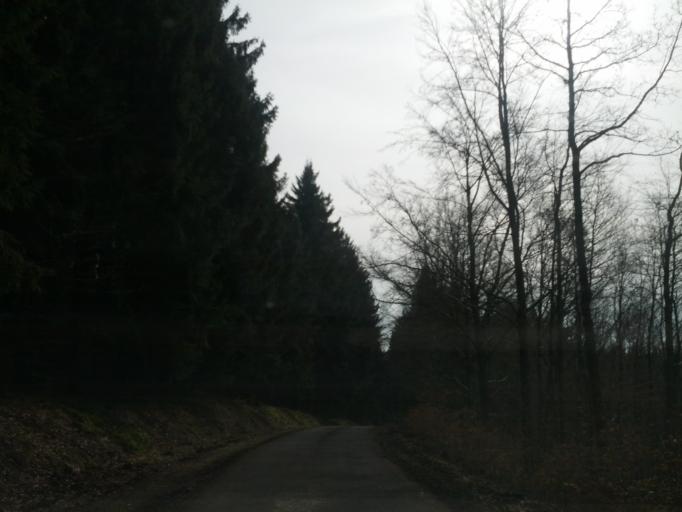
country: DE
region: Thuringia
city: Schweina
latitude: 50.8513
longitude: 10.3178
